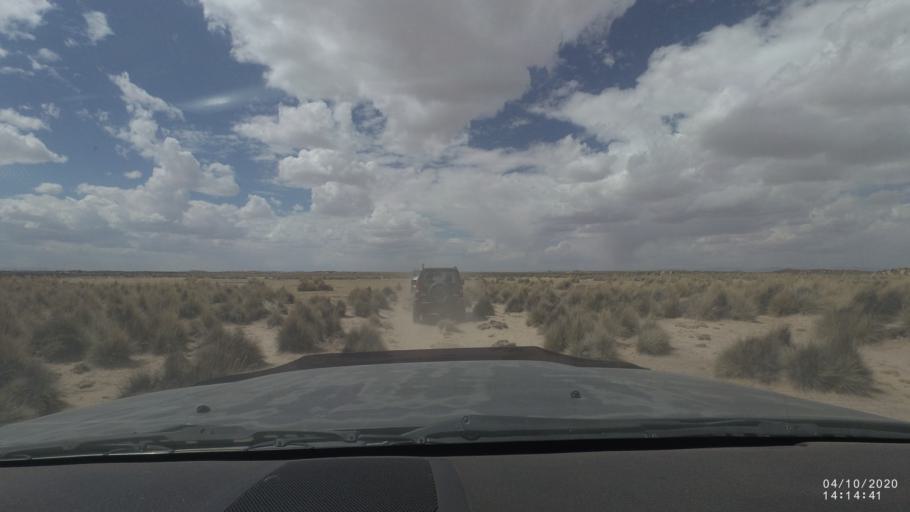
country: BO
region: Oruro
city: Poopo
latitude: -18.6946
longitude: -67.4545
